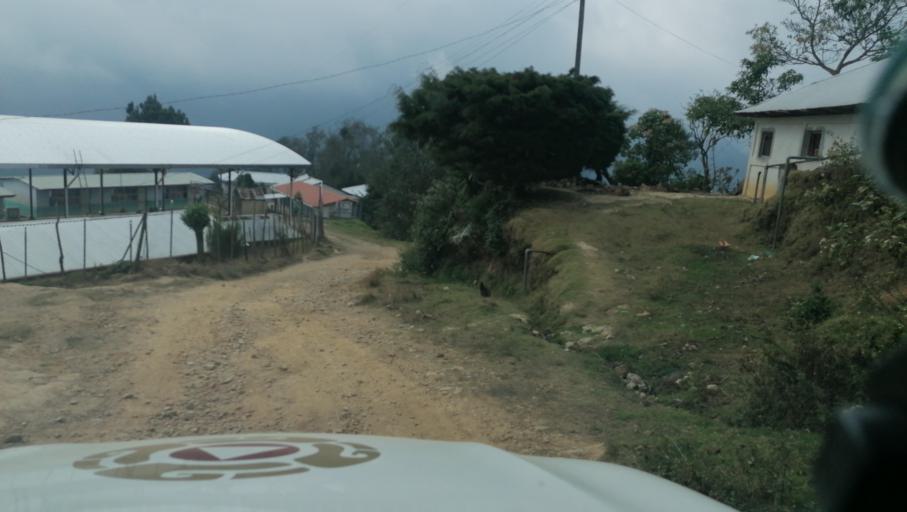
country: GT
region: San Marcos
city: Tacana
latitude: 15.2181
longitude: -92.1931
